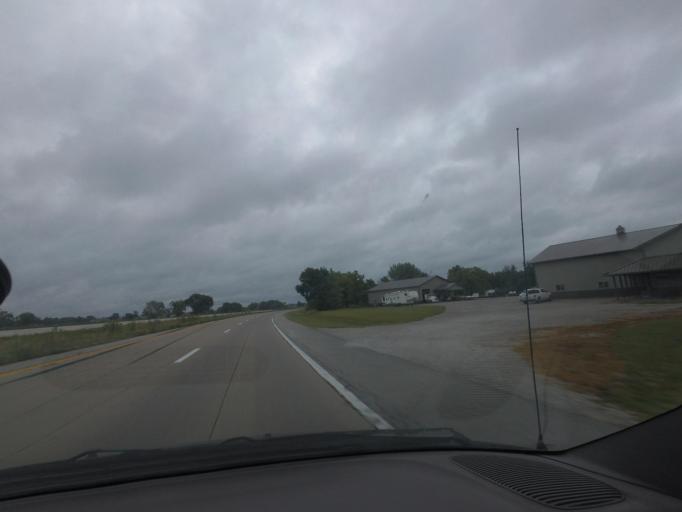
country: US
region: Missouri
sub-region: Marion County
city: Monroe City
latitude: 39.6731
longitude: -91.8598
